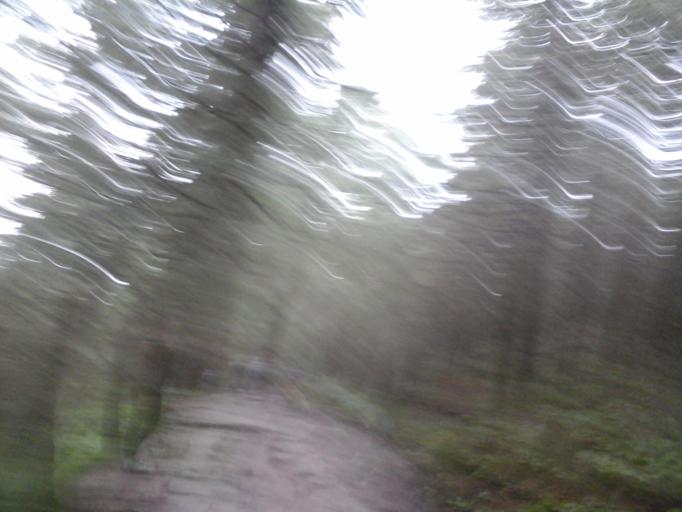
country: PL
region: Lesser Poland Voivodeship
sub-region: Powiat tatrzanski
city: Zakopane
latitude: 49.2640
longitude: 19.9934
